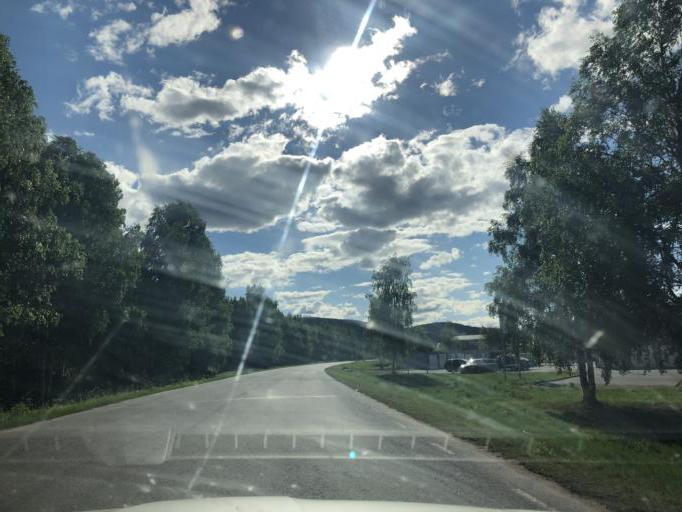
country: SE
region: Norrbotten
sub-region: Overkalix Kommun
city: OEverkalix
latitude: 66.3223
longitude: 22.8550
